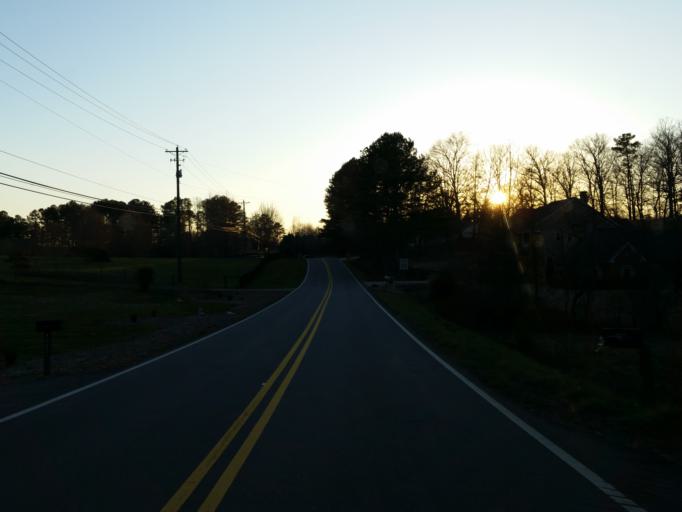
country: US
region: Georgia
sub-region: Cherokee County
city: Holly Springs
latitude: 34.1245
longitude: -84.4283
